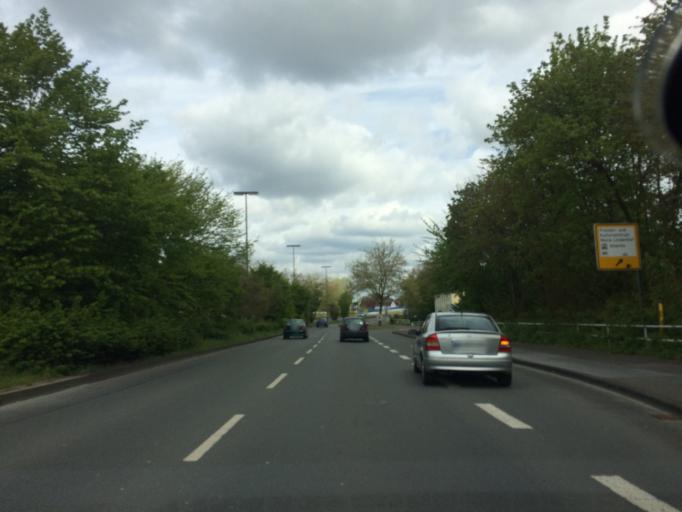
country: DE
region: North Rhine-Westphalia
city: Dorsten
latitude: 51.6648
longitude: 6.9656
